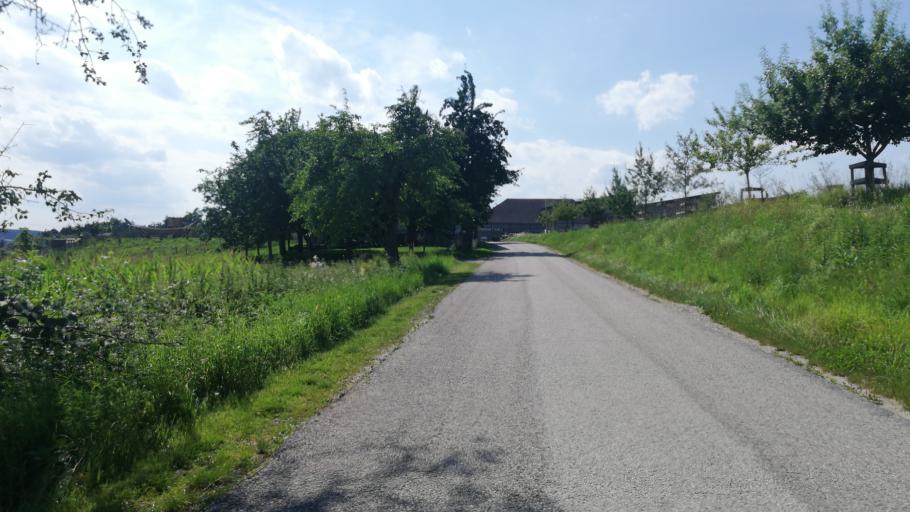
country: AT
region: Upper Austria
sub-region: Wels-Land
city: Pennewang
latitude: 48.1604
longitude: 13.8788
